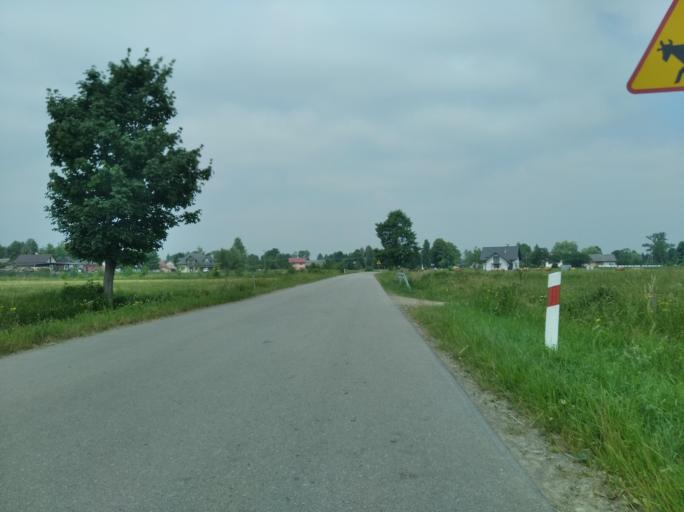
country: PL
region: Subcarpathian Voivodeship
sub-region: Powiat sanocki
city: Besko
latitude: 49.6145
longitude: 21.9477
